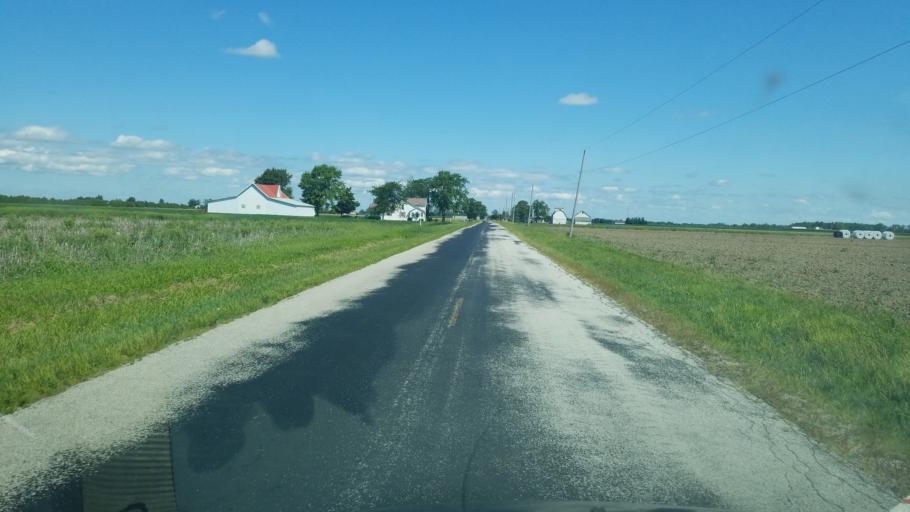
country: US
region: Ohio
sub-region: Henry County
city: Deshler
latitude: 41.2576
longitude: -83.8433
